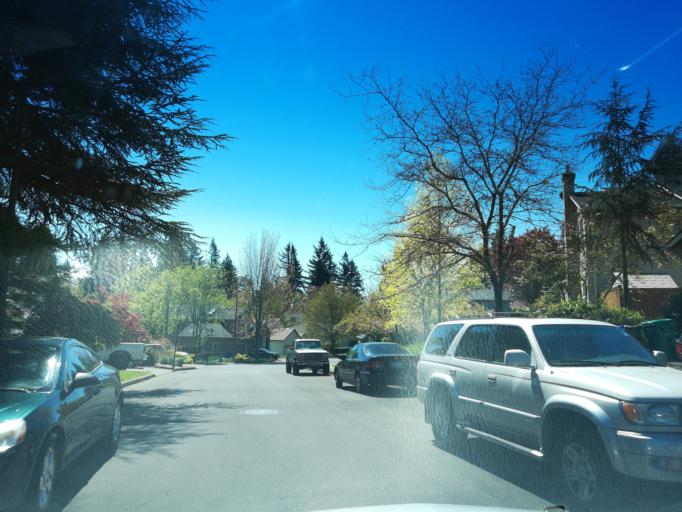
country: US
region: Oregon
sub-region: Multnomah County
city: Troutdale
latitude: 45.5070
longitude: -122.3913
